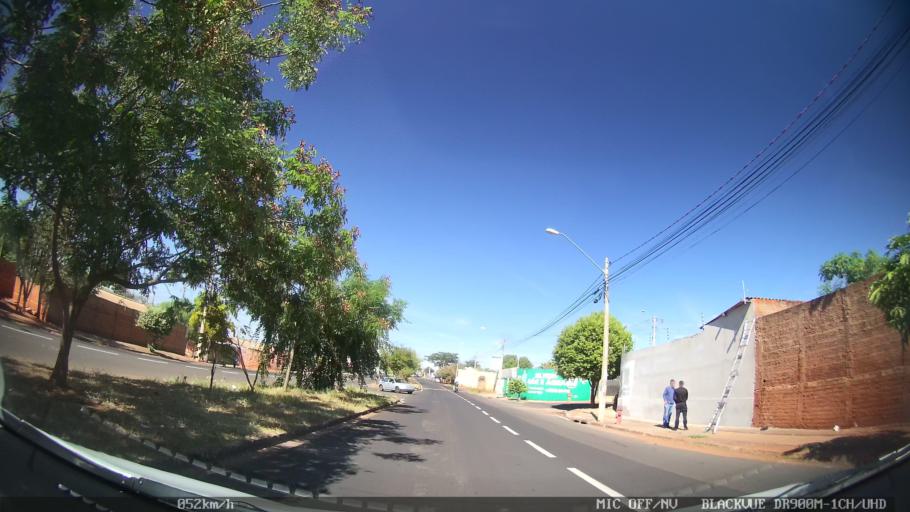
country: BR
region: Sao Paulo
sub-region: Sao Jose Do Rio Preto
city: Sao Jose do Rio Preto
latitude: -20.7452
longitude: -49.4085
